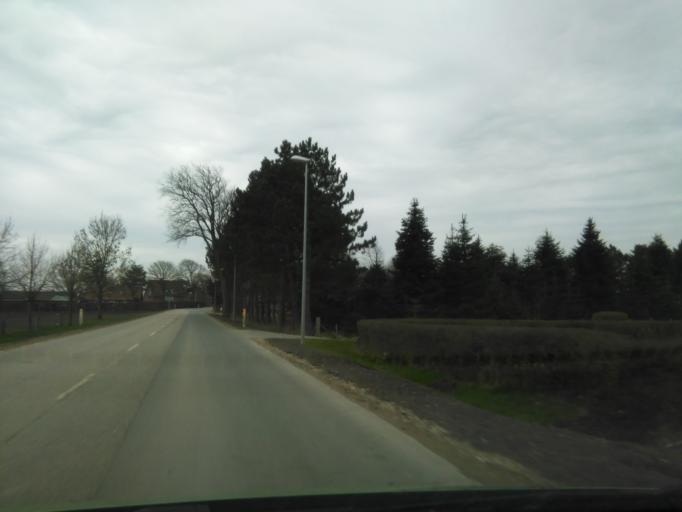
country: DK
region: Central Jutland
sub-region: Randers Kommune
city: Spentrup
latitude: 56.5496
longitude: 10.0017
